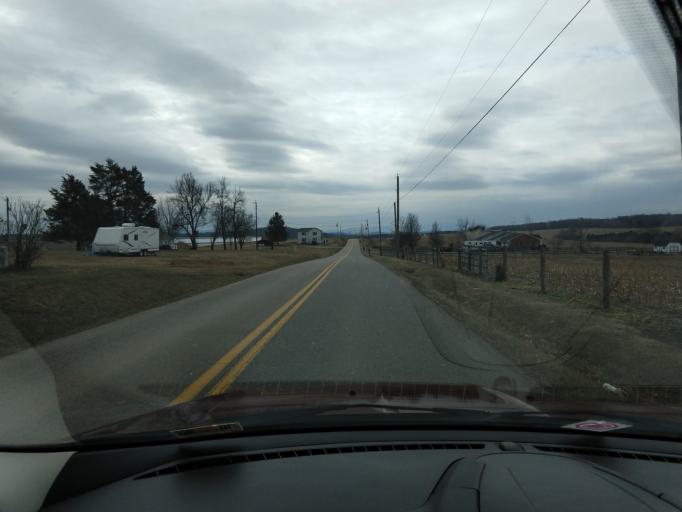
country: US
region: Virginia
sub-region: Augusta County
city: Crimora
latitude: 38.1647
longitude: -78.9199
